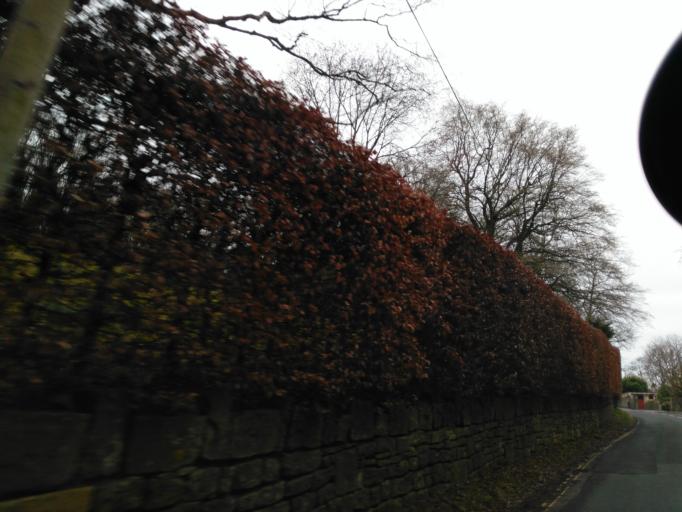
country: GB
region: England
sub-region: Bath and North East Somerset
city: Bath
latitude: 51.3805
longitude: -2.3399
